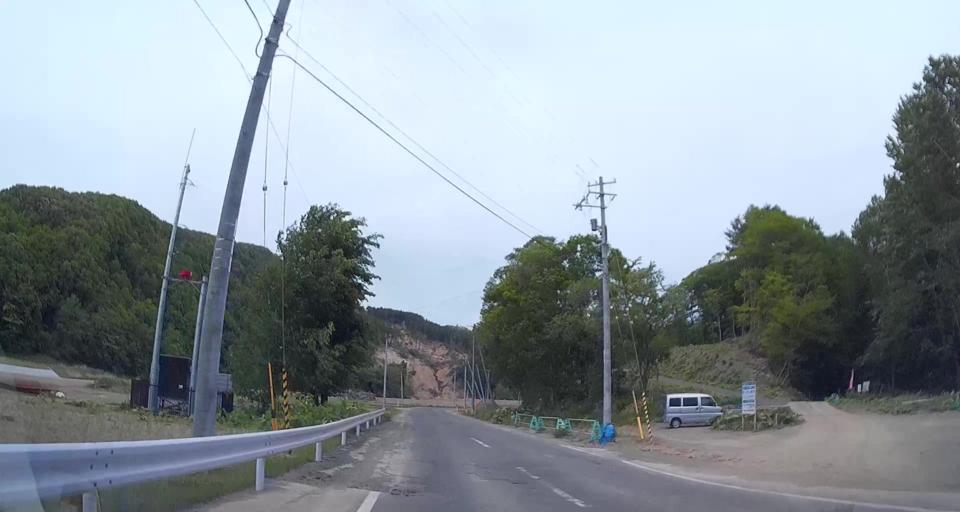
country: JP
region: Hokkaido
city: Chitose
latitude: 42.7606
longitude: 141.9798
